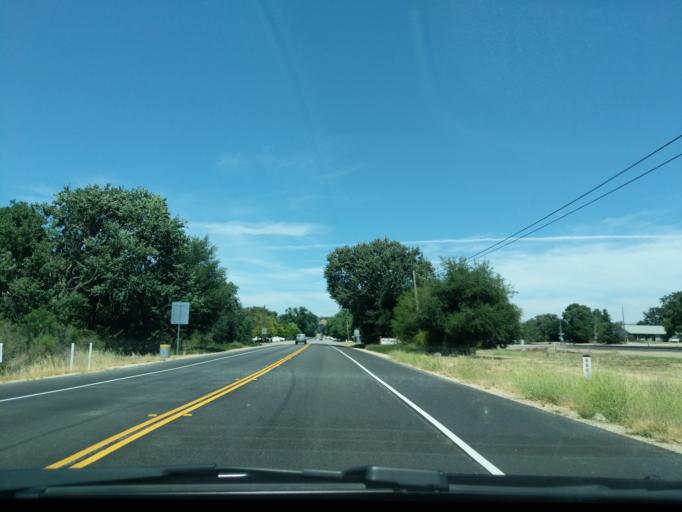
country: US
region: California
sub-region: San Luis Obispo County
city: Santa Margarita
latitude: 35.3856
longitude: -120.6187
